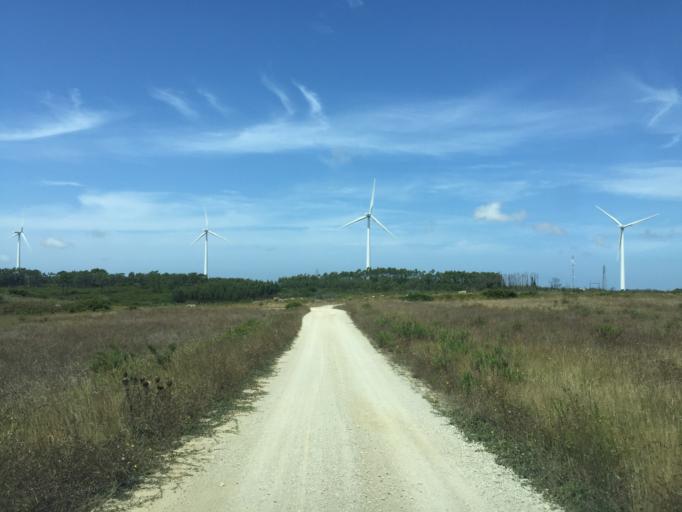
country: PT
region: Leiria
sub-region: Peniche
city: Atouguia da Baleia
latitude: 39.3170
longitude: -9.2587
